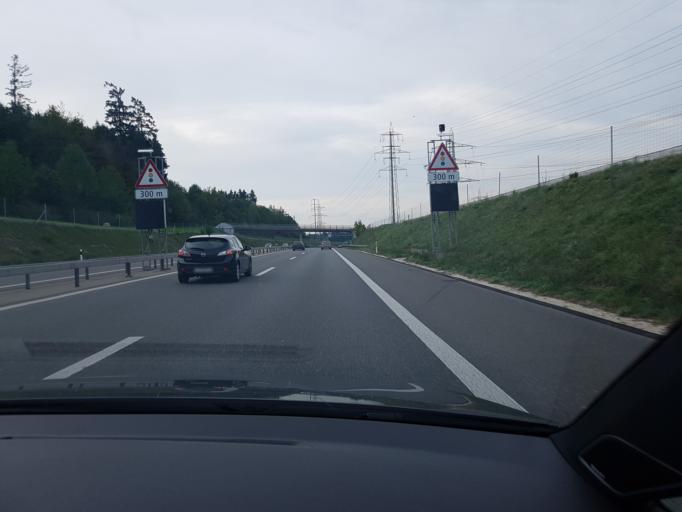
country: CH
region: Zurich
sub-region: Bezirk Affoltern
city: Obfelden / Toussen
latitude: 47.2824
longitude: 8.4260
